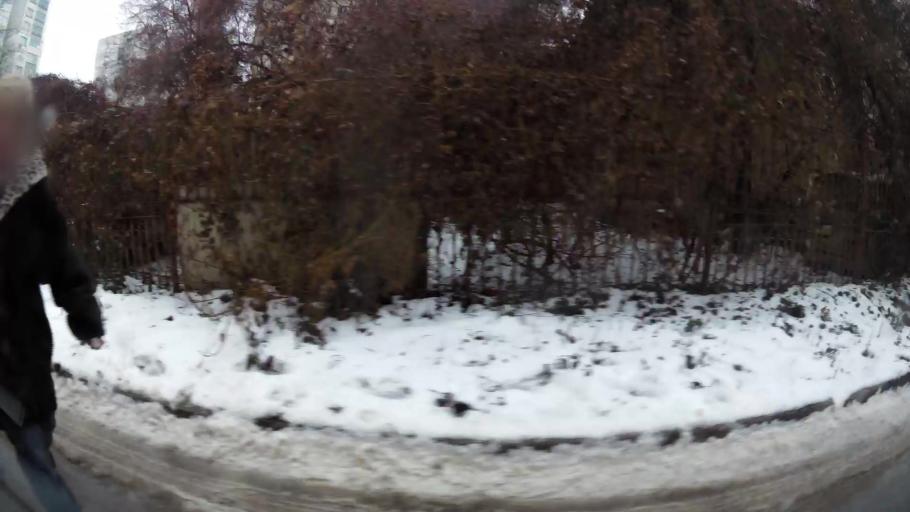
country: BG
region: Sofia-Capital
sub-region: Stolichna Obshtina
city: Sofia
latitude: 42.6674
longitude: 23.2720
